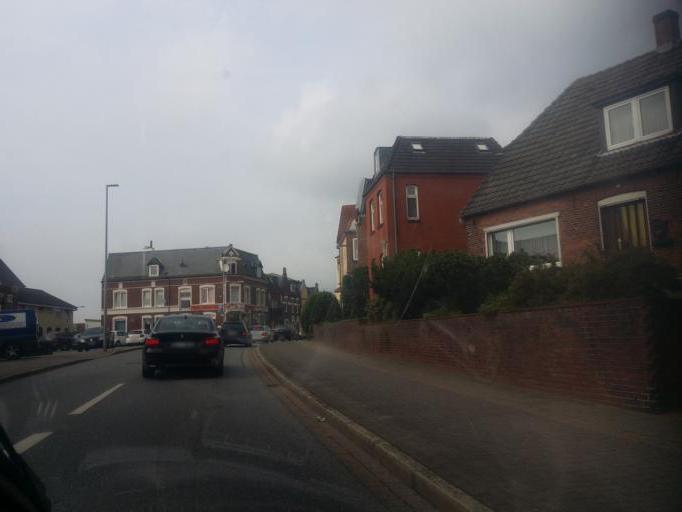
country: DE
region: Schleswig-Holstein
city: Husum
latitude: 54.4702
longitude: 9.0519
